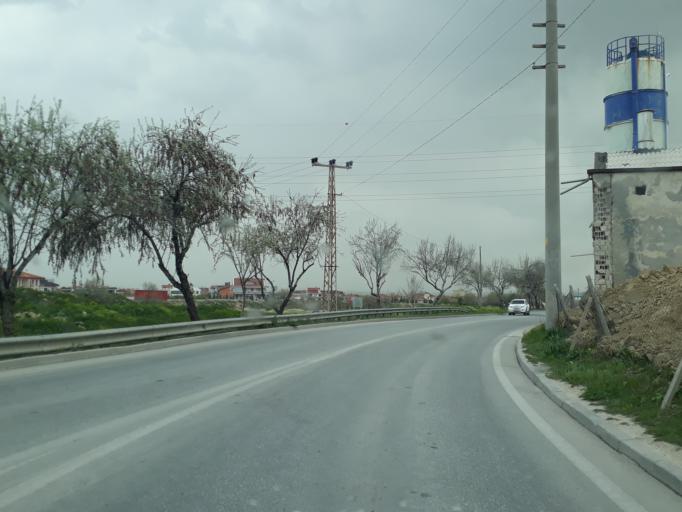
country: TR
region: Konya
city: Selcuklu
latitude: 37.9200
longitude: 32.4680
